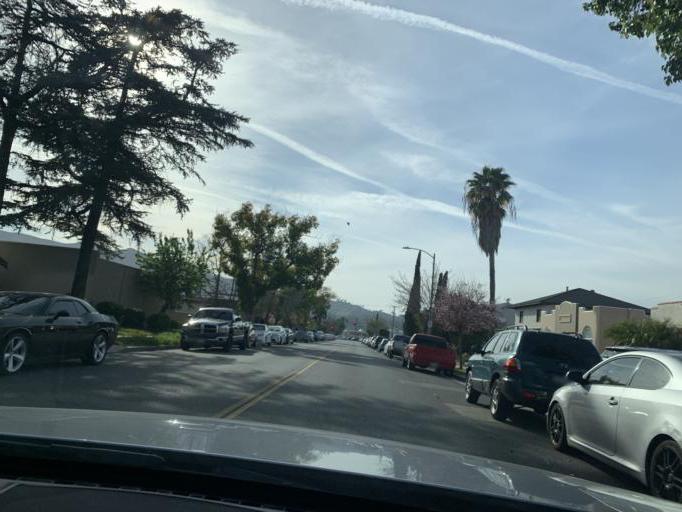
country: US
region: California
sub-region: Los Angeles County
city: North Glendale
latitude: 34.1480
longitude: -118.2691
